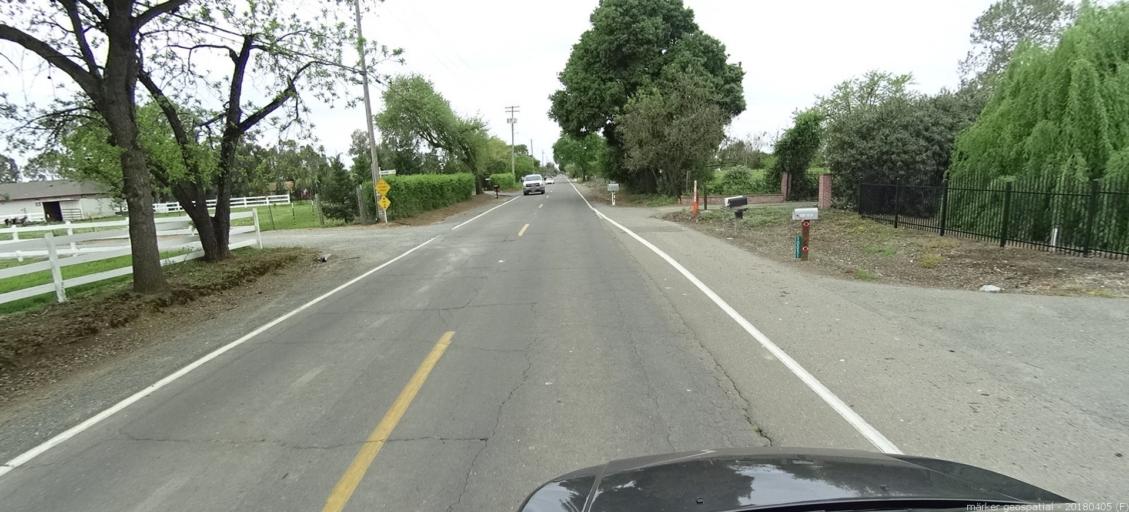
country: US
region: California
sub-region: Sacramento County
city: Galt
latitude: 38.2474
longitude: -121.3215
